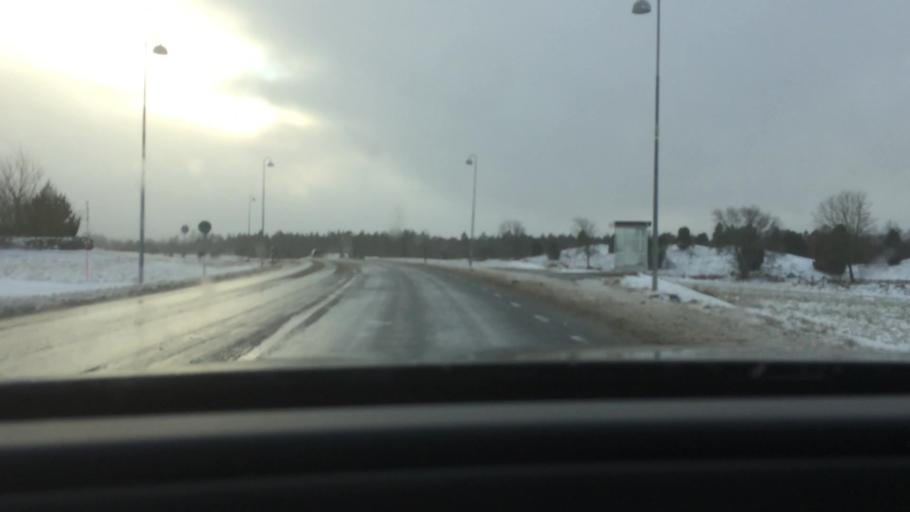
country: SE
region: Vaestra Goetaland
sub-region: Falkopings Kommun
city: Falkoeping
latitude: 57.9798
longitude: 13.5276
